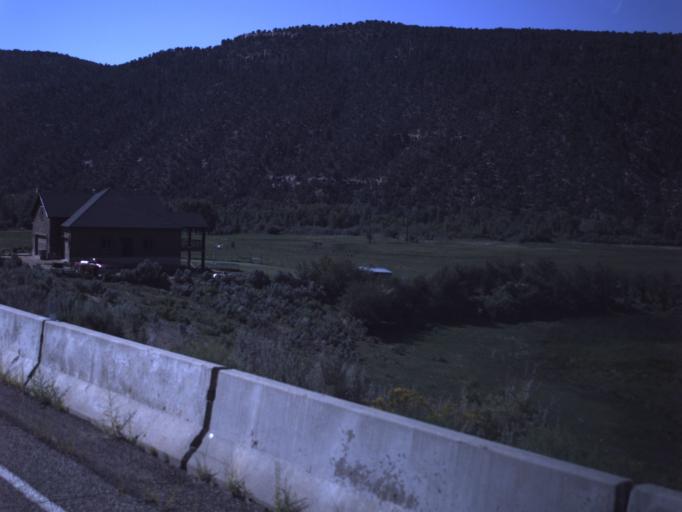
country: US
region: Utah
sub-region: Duchesne County
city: Duchesne
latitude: 40.3116
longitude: -110.6394
